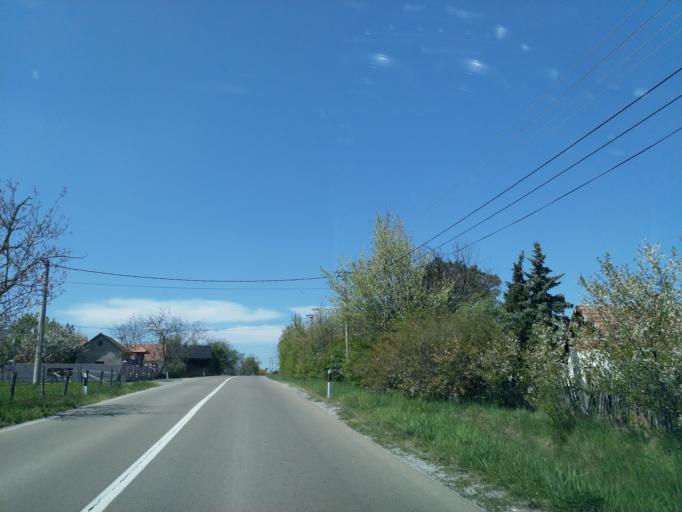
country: RS
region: Central Serbia
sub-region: Belgrade
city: Lazarevac
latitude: 44.3492
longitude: 20.3849
